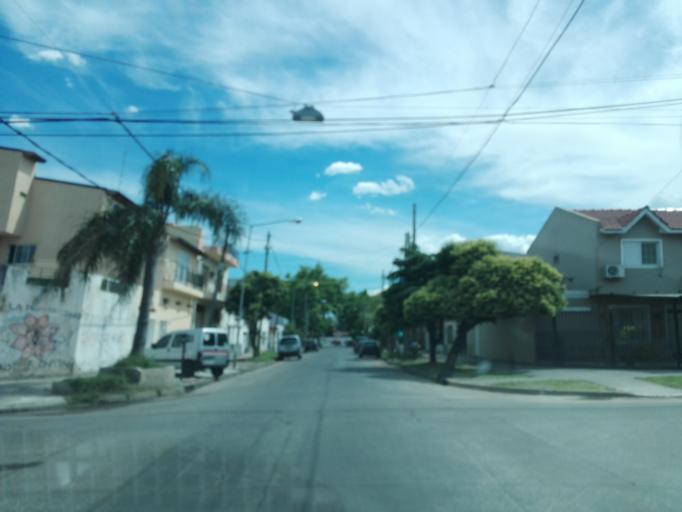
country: AR
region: Buenos Aires
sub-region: Partido de Lanus
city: Lanus
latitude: -34.7241
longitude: -58.3889
